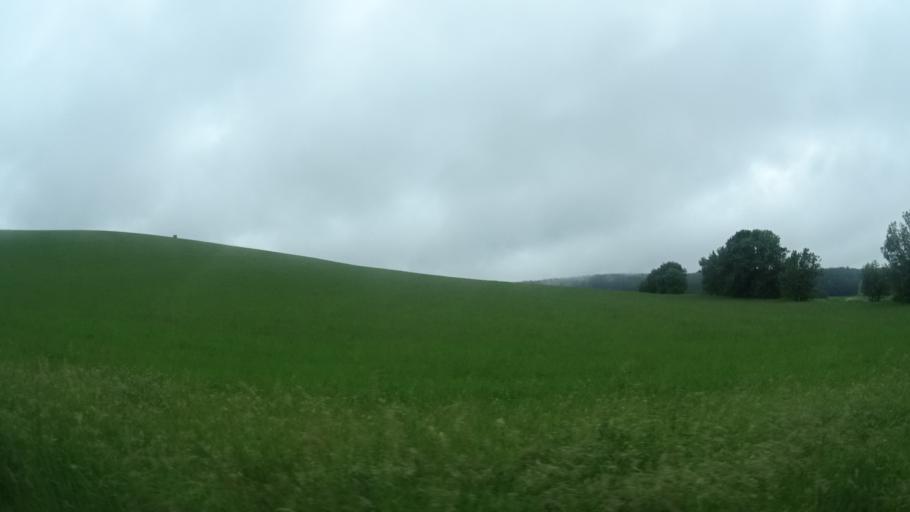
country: DE
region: Thuringia
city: Langewiesen
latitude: 50.6785
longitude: 10.9581
